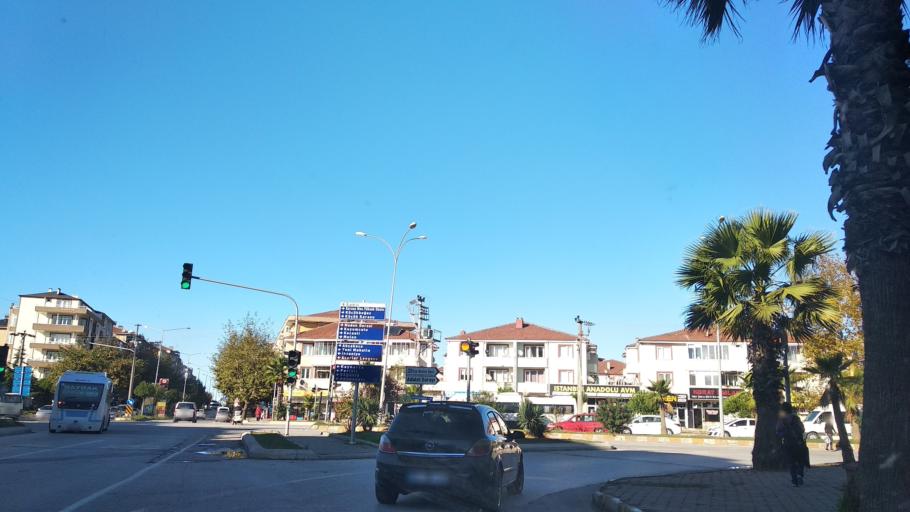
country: TR
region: Sakarya
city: Karasu
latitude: 41.1046
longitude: 30.6927
